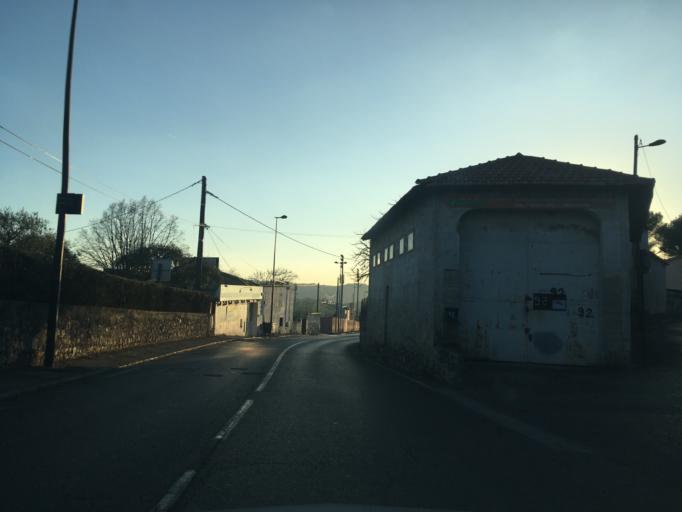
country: FR
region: Provence-Alpes-Cote d'Azur
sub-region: Departement des Alpes-Maritimes
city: Grasse
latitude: 43.6440
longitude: 6.9138
